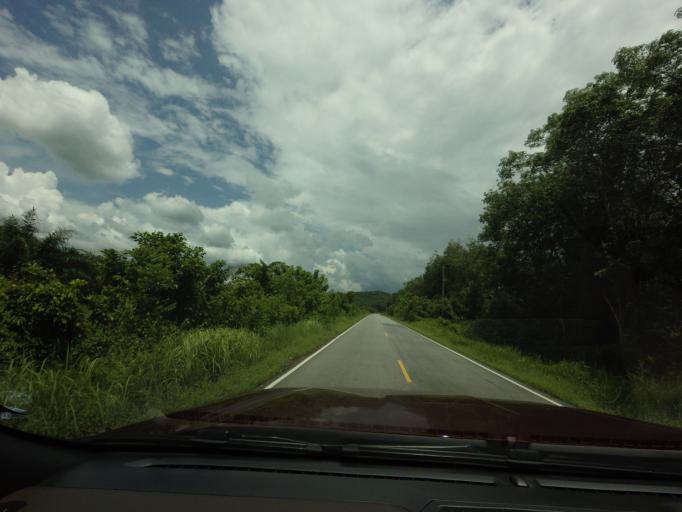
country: TH
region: Narathiwat
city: Chanae
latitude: 6.0579
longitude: 101.6877
